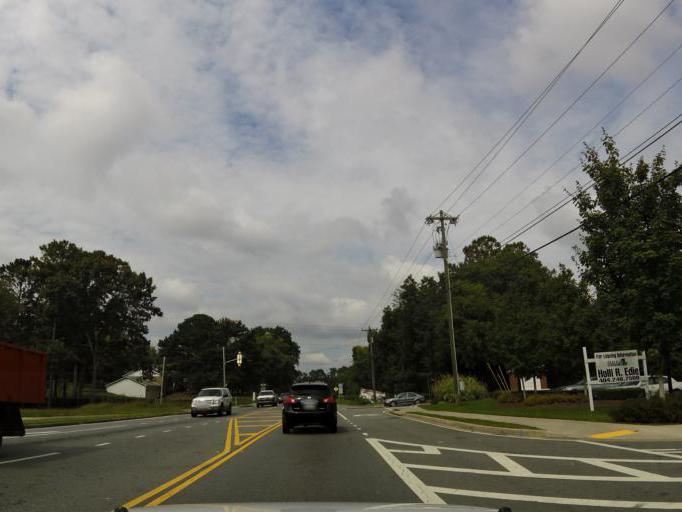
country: US
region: Georgia
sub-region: Cobb County
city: Kennesaw
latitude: 33.9927
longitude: -84.6286
